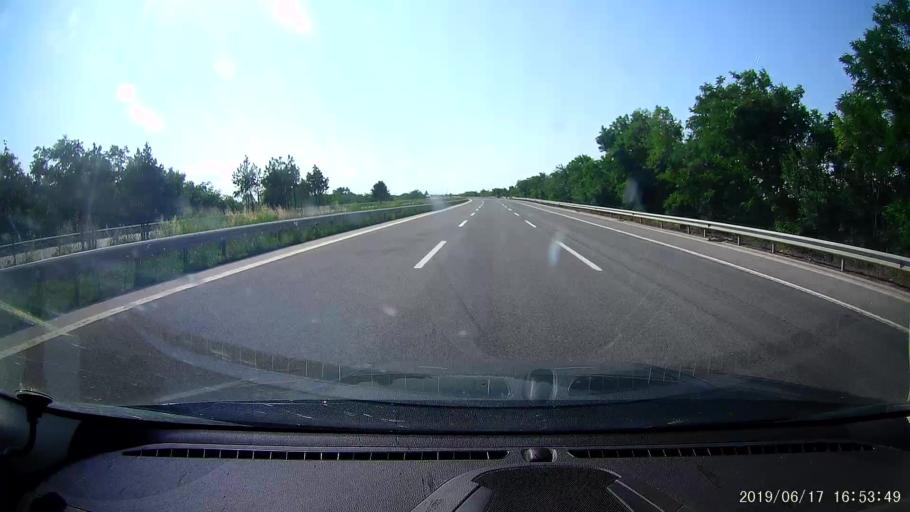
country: TR
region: Kirklareli
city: Inece
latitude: 41.5682
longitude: 27.0137
